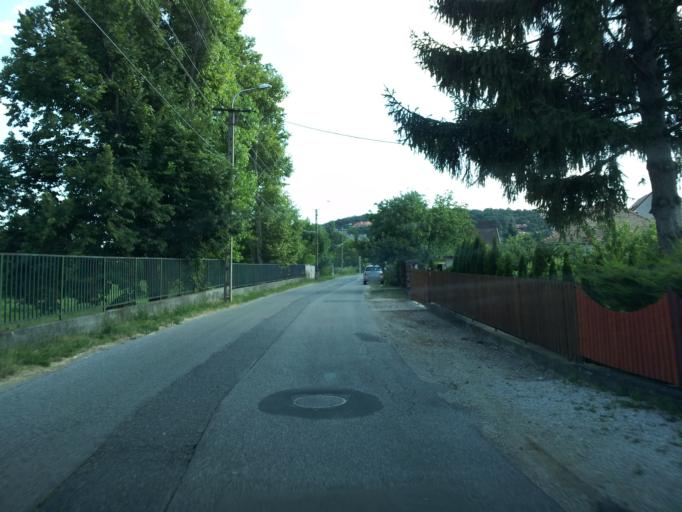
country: HU
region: Veszprem
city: Balatonalmadi
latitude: 47.0213
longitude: 18.0063
